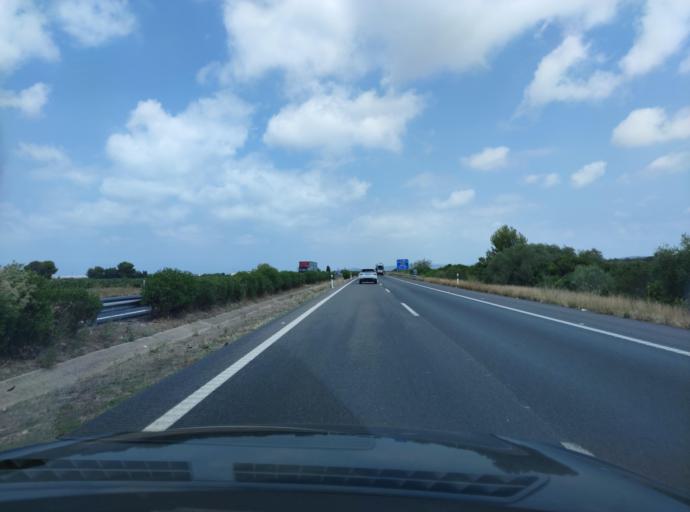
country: ES
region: Valencia
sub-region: Provincia de Castello
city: Vinaros
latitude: 40.5105
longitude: 0.4154
